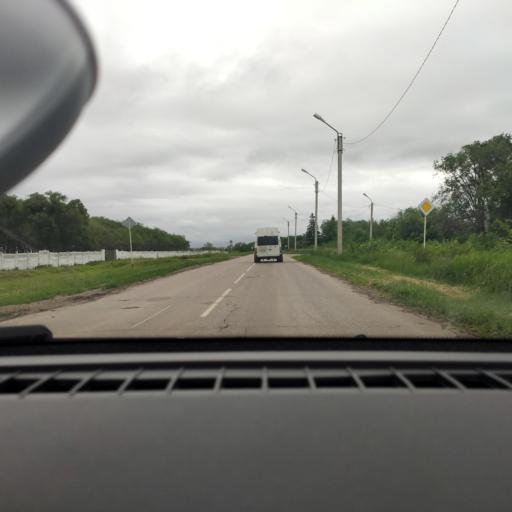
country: RU
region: Samara
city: Spiridonovka
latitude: 53.0574
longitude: 50.4789
